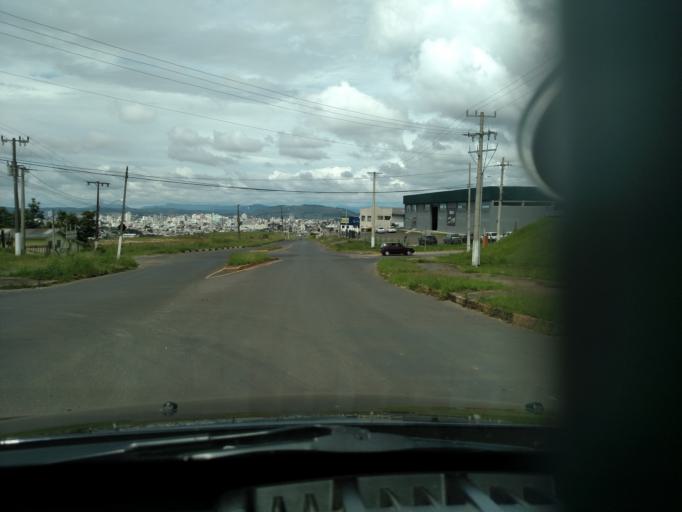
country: BR
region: Santa Catarina
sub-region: Lages
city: Lages
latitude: -27.8189
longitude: -50.3627
